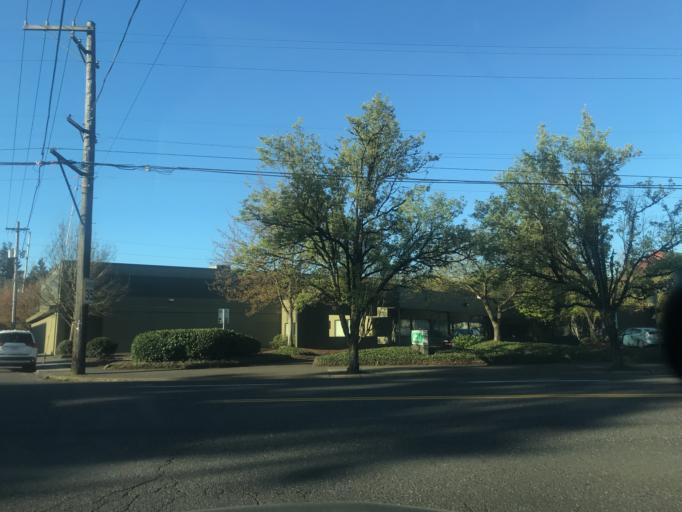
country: US
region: Oregon
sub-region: Multnomah County
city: Lents
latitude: 45.4843
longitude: -122.5822
